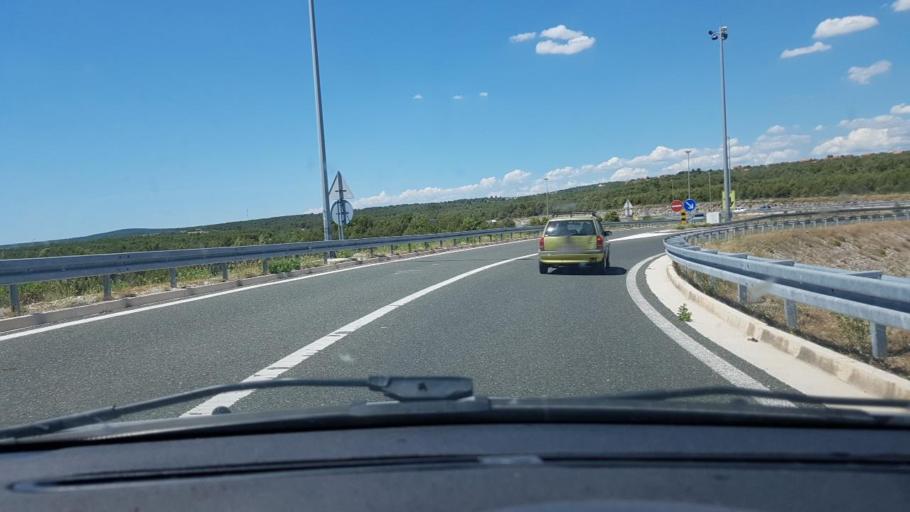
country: HR
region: Sibensko-Kniniska
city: Zaton
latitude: 43.8361
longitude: 15.8846
